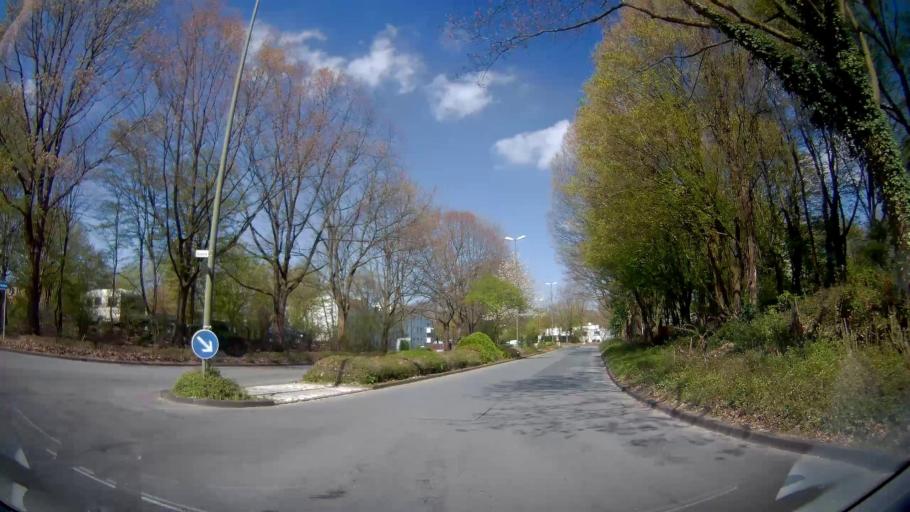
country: DE
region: North Rhine-Westphalia
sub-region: Regierungsbezirk Munster
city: Klein Reken
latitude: 51.7274
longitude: 7.0415
